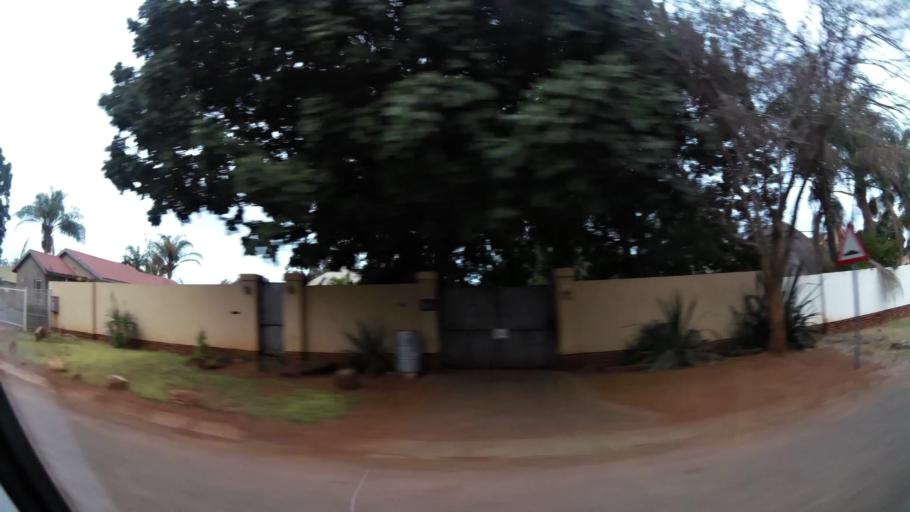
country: ZA
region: Limpopo
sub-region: Waterberg District Municipality
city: Mokopane
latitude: -24.1838
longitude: 28.9921
